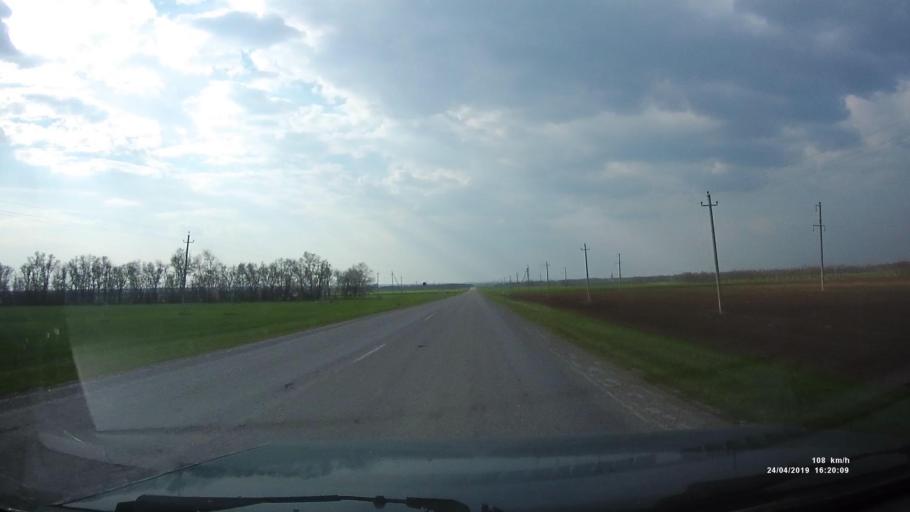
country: RU
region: Rostov
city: Orlovskiy
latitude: 46.7888
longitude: 42.0854
